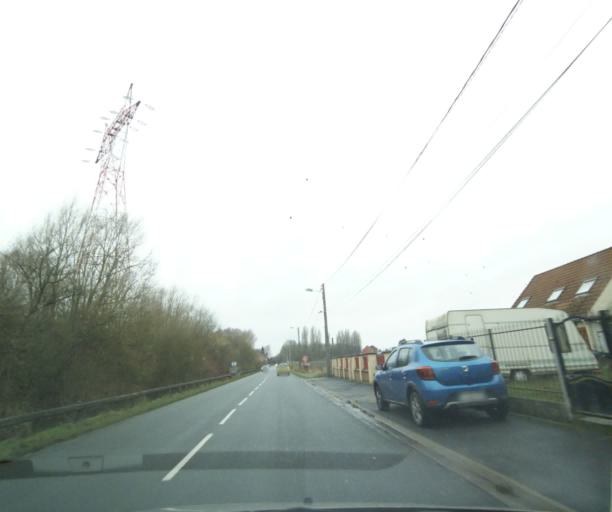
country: FR
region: Nord-Pas-de-Calais
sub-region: Departement du Nord
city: Haulchin
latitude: 50.3287
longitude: 3.4297
